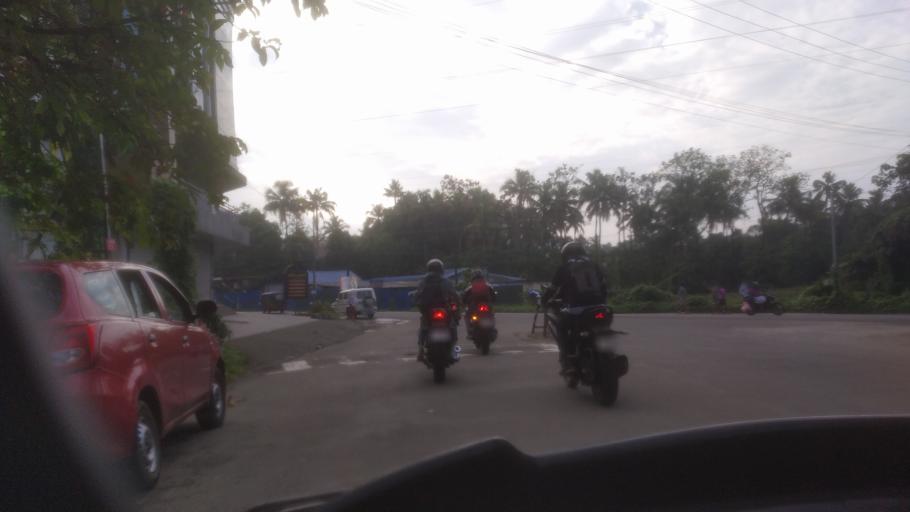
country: IN
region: Kerala
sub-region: Ernakulam
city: Kotamangalam
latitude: 10.0606
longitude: 76.6349
